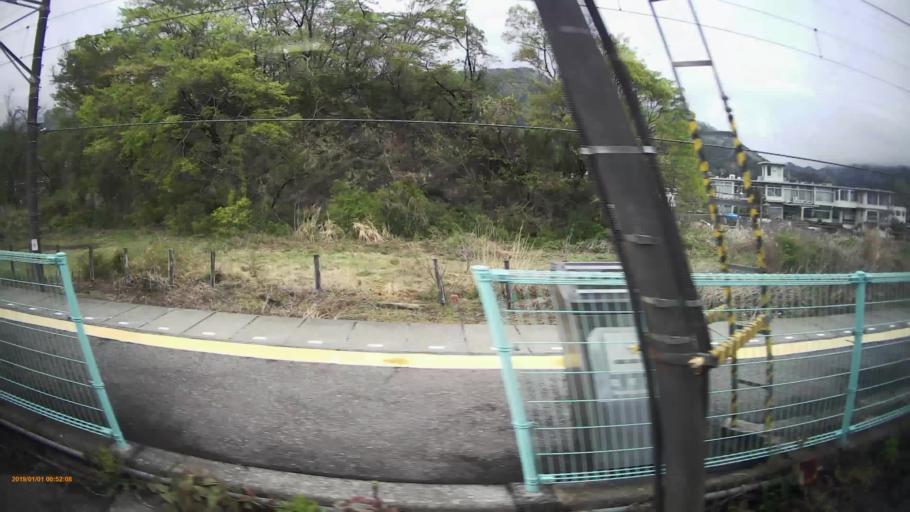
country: JP
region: Yamanashi
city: Otsuki
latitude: 35.5943
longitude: 138.8831
